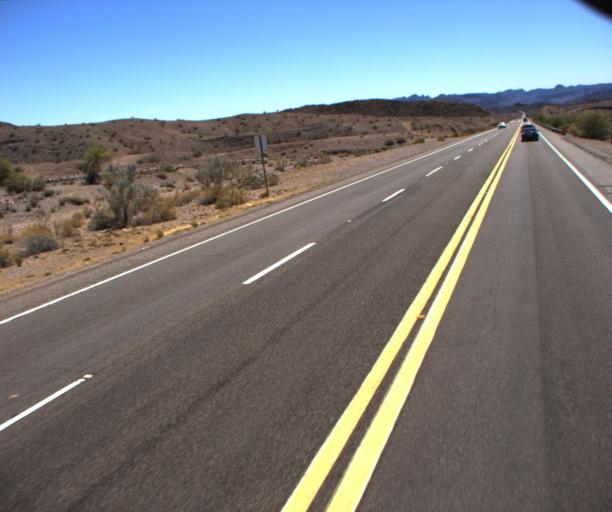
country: US
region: Arizona
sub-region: Mohave County
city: Lake Havasu City
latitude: 34.3837
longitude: -114.1665
